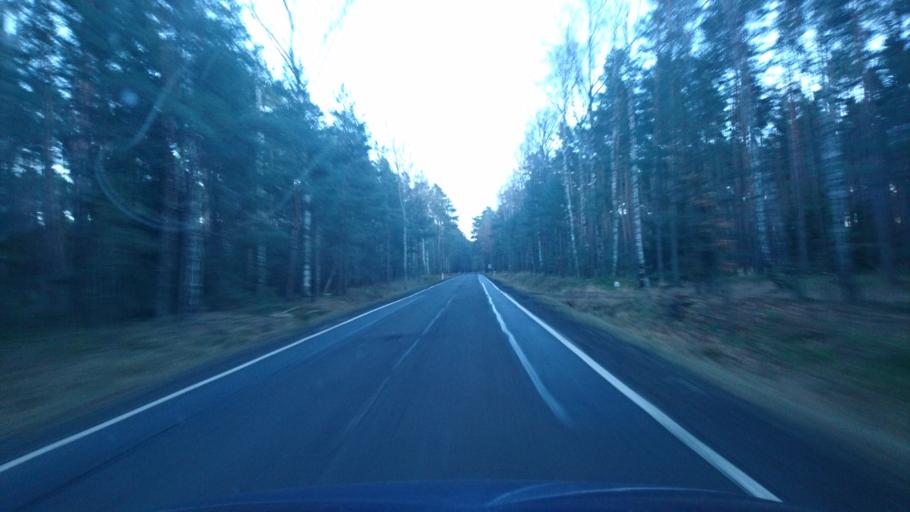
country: PL
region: Greater Poland Voivodeship
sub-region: Powiat ostrowski
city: Odolanow
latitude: 51.5340
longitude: 17.7394
